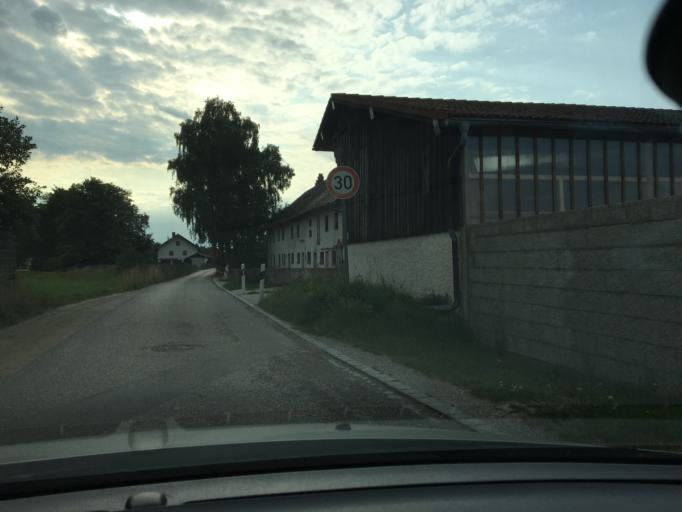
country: DE
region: Bavaria
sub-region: Upper Bavaria
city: Muehldorf
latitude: 48.2531
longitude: 12.5469
